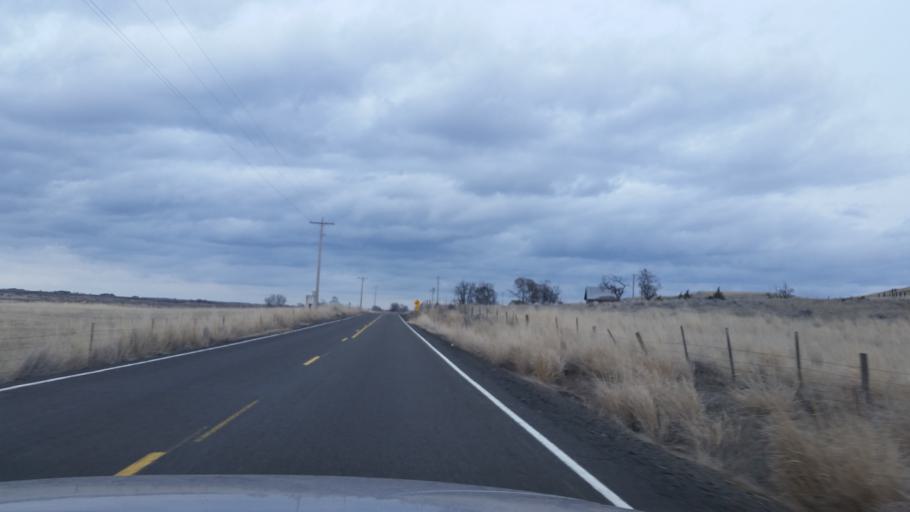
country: US
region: Washington
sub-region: Spokane County
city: Medical Lake
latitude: 47.1898
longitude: -117.9215
